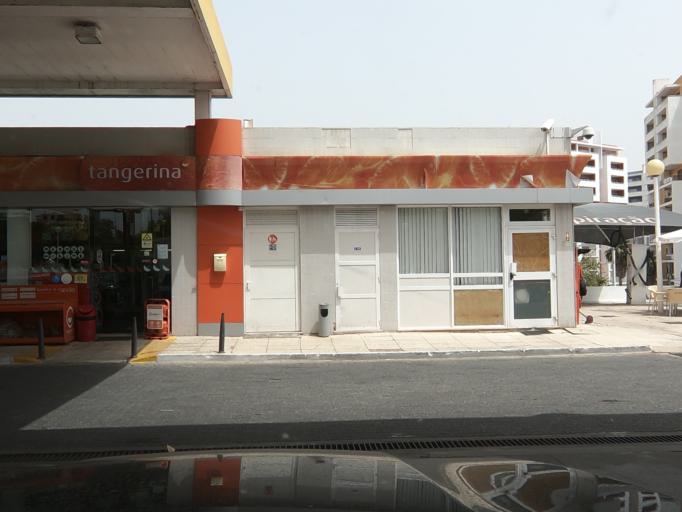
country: PT
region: Faro
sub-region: Portimao
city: Portimao
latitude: 37.1293
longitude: -8.5484
